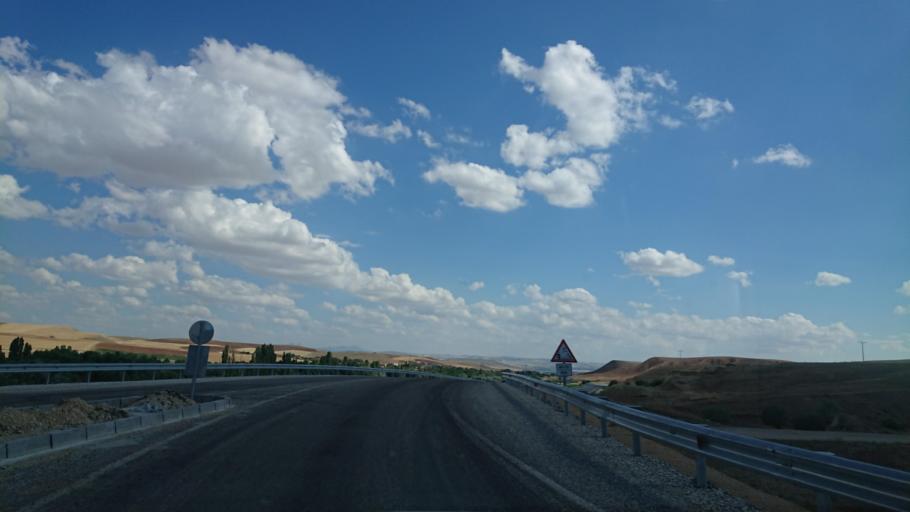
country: TR
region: Ankara
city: Evren
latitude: 39.1014
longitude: 33.9063
